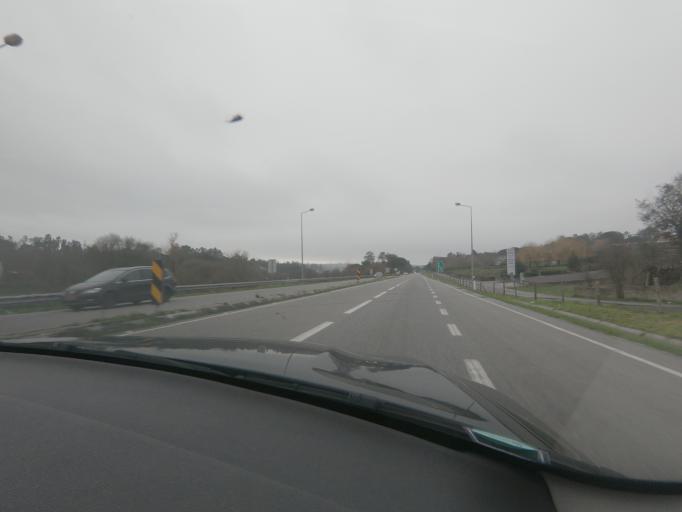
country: PT
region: Viseu
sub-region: Concelho de Tondela
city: Tondela
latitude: 40.5344
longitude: -8.0614
